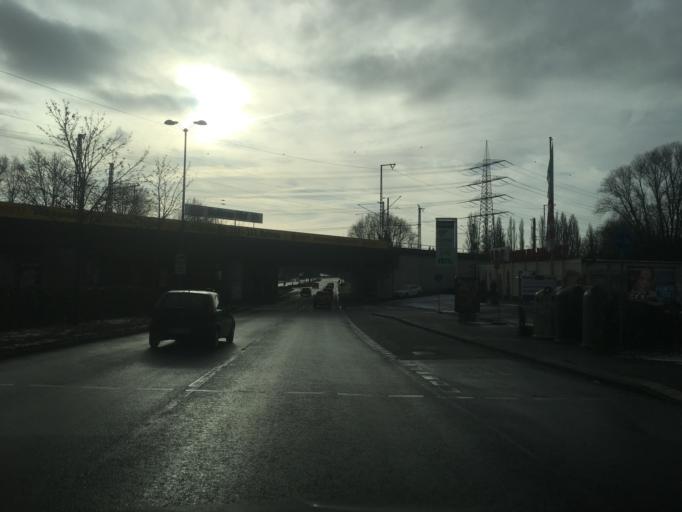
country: DE
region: North Rhine-Westphalia
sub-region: Regierungsbezirk Munster
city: Bottrop
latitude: 51.5089
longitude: 6.9350
